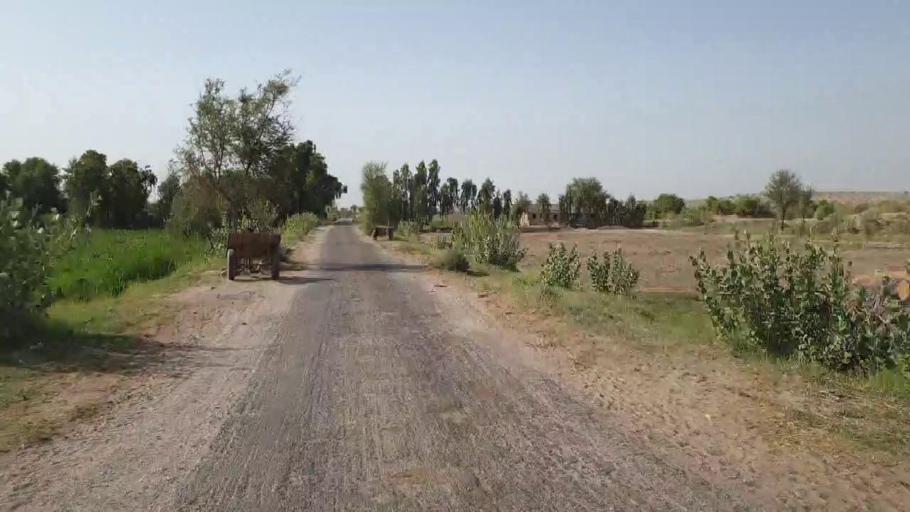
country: PK
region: Sindh
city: Kandiari
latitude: 26.6978
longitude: 68.9646
